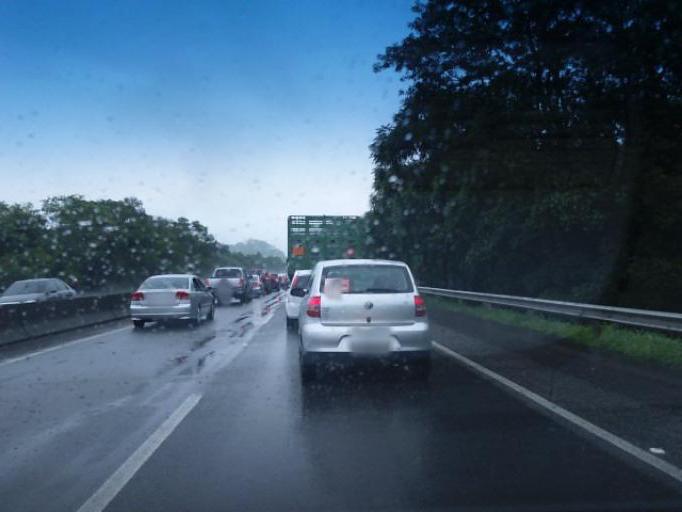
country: BR
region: Santa Catarina
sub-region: Joinville
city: Joinville
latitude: -26.1239
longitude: -48.8846
